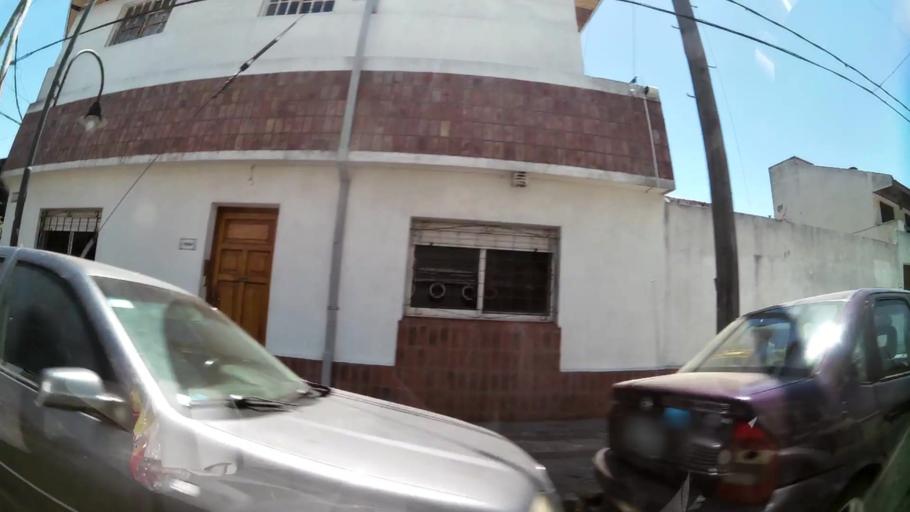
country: AR
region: Buenos Aires
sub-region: Partido de Tigre
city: Tigre
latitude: -34.4463
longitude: -58.5481
